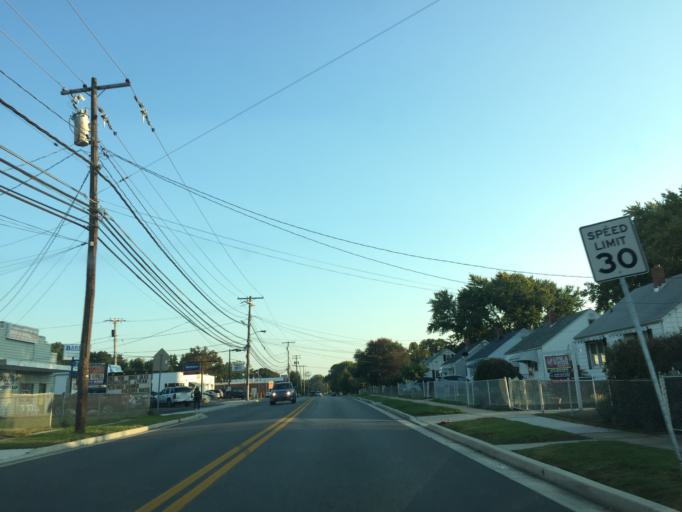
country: US
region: Maryland
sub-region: Baltimore County
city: Essex
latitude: 39.3042
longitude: -76.4631
